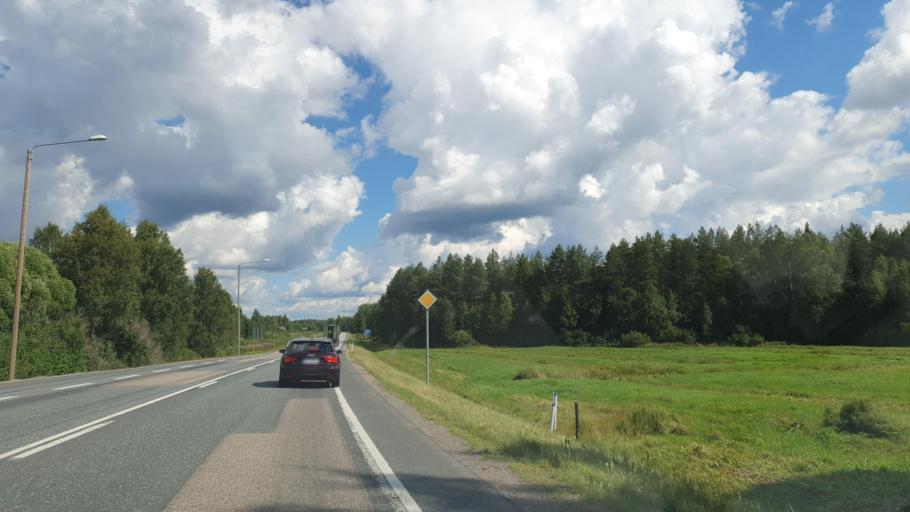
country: FI
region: Kainuu
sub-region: Kajaani
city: Kajaani
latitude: 64.1195
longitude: 27.4534
